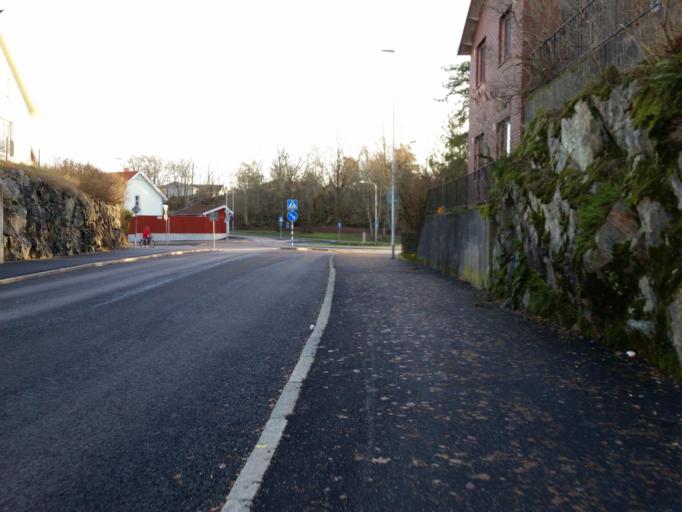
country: SE
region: Vaestra Goetaland
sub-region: Trollhattan
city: Trollhattan
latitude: 58.2820
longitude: 12.2671
